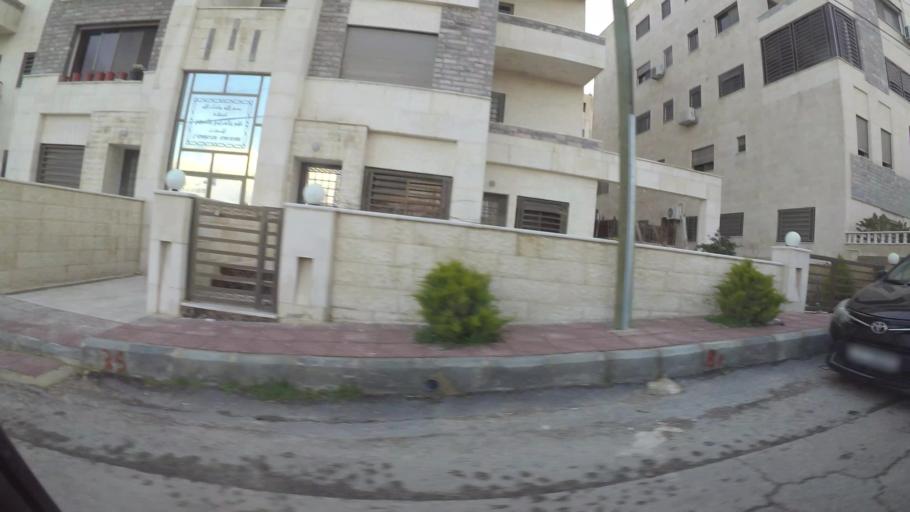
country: JO
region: Amman
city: Al Jubayhah
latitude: 32.0475
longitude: 35.8946
